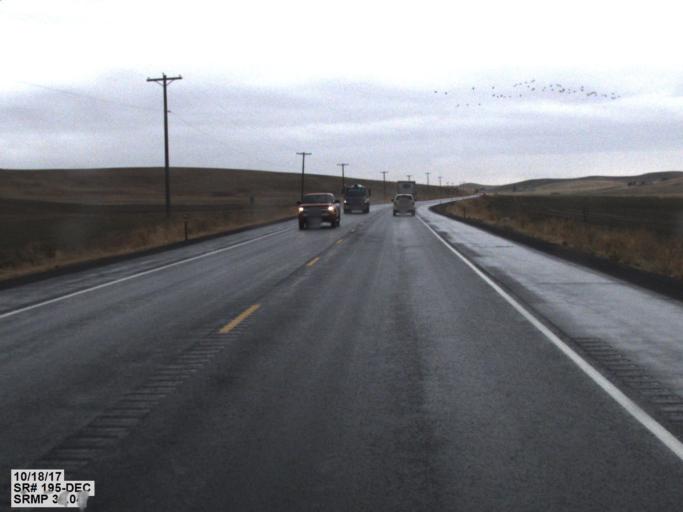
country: US
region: Washington
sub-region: Whitman County
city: Colfax
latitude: 46.8113
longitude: -117.3200
